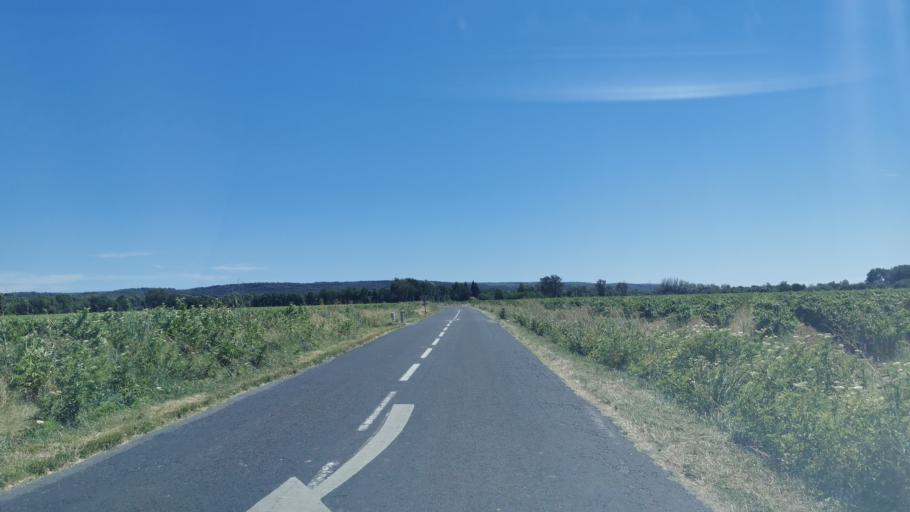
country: FR
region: Languedoc-Roussillon
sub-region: Departement de l'Aude
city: Coursan
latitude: 43.2328
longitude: 3.0763
